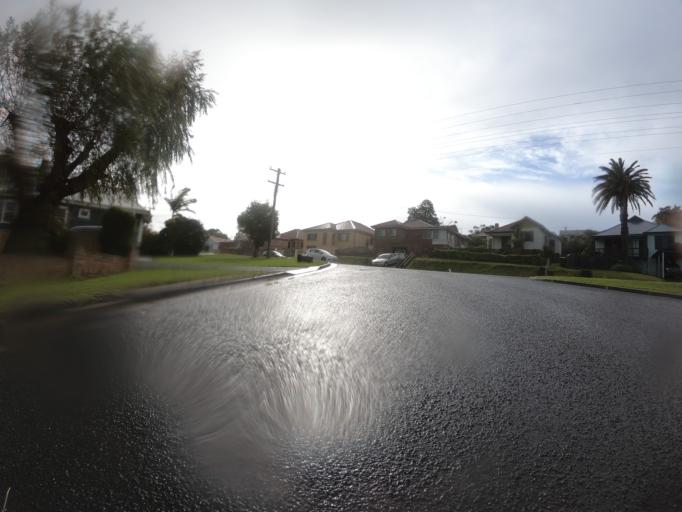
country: AU
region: New South Wales
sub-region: Wollongong
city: Port Kembla
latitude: -34.4870
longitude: 150.8977
